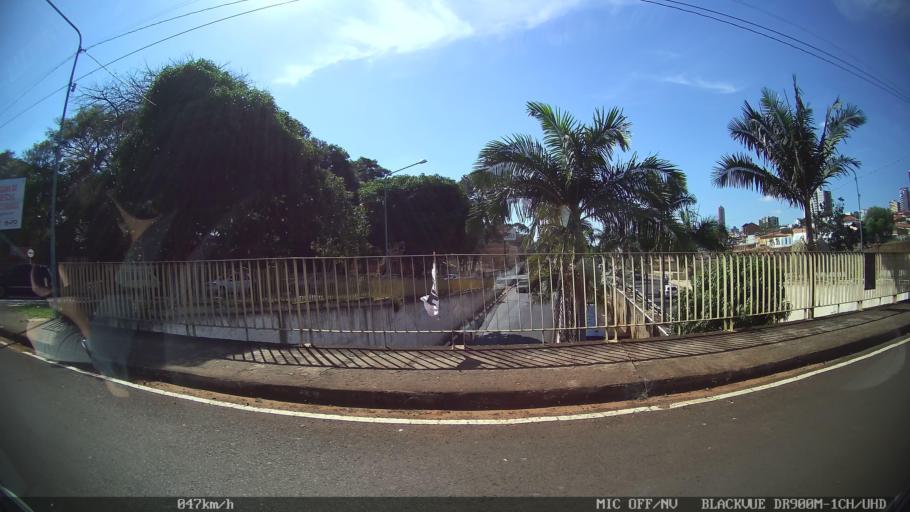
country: BR
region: Sao Paulo
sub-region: Franca
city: Franca
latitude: -20.5337
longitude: -47.4054
